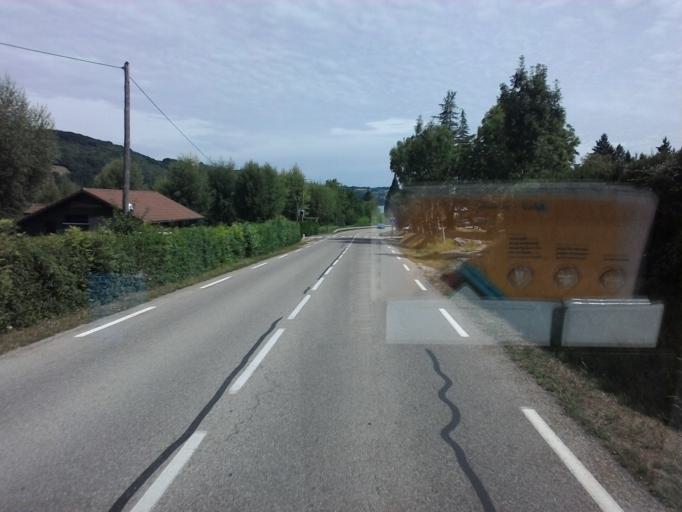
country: FR
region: Rhone-Alpes
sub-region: Departement de l'Isere
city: Bilieu
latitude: 45.4456
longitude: 5.5312
